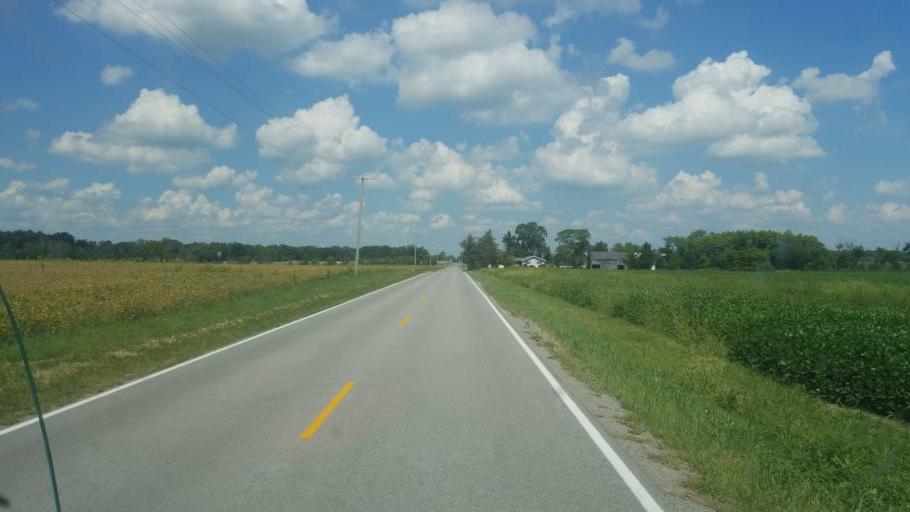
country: US
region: Ohio
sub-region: Hancock County
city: Arlington
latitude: 40.8851
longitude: -83.7271
